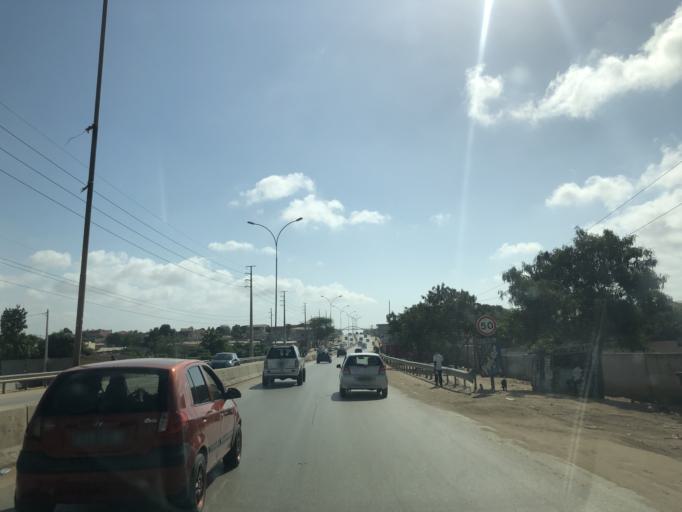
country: AO
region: Luanda
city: Luanda
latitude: -8.9058
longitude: 13.2445
